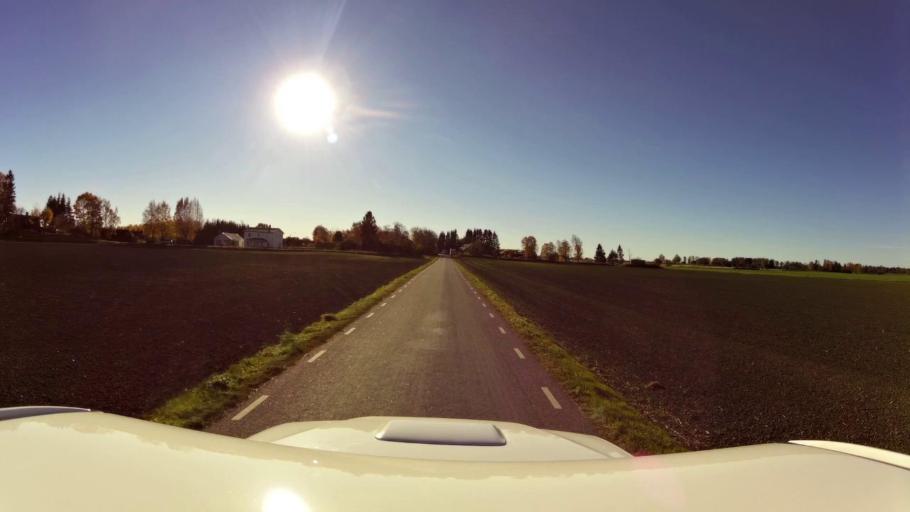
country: SE
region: OEstergoetland
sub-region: Linkopings Kommun
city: Ljungsbro
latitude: 58.4952
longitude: 15.4192
